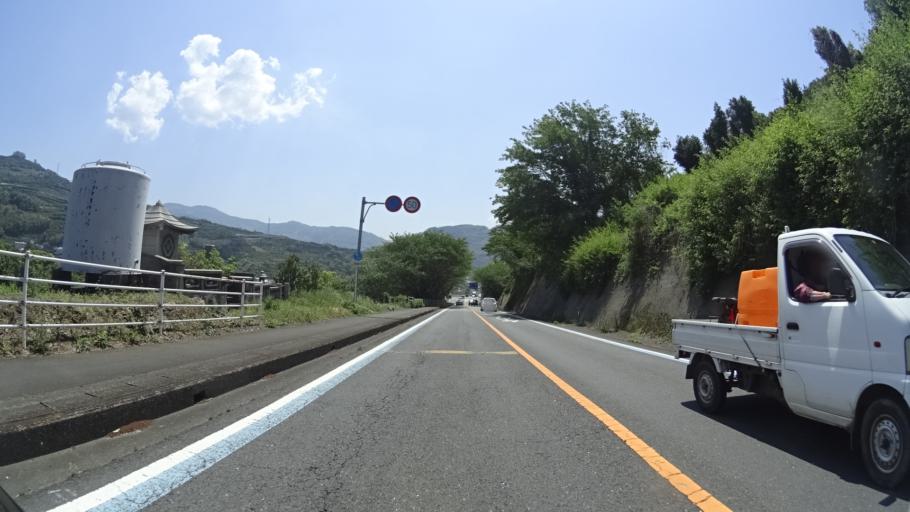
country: JP
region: Ehime
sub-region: Nishiuwa-gun
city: Ikata-cho
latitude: 33.4902
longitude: 132.3954
